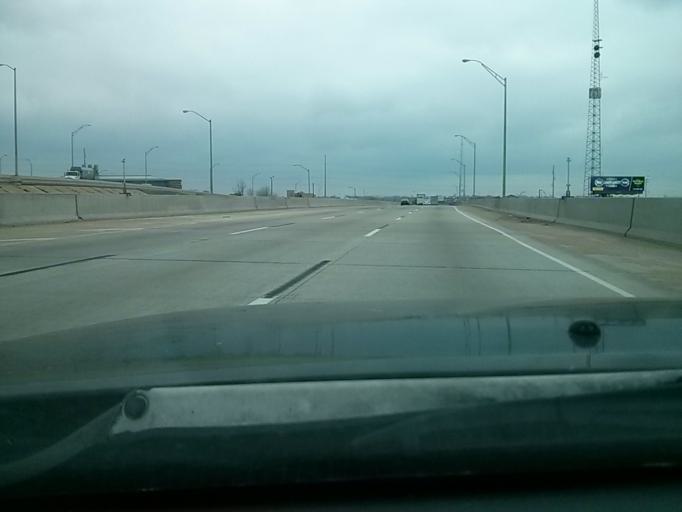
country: US
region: Oklahoma
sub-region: Tulsa County
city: Tulsa
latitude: 36.1614
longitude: -95.9946
